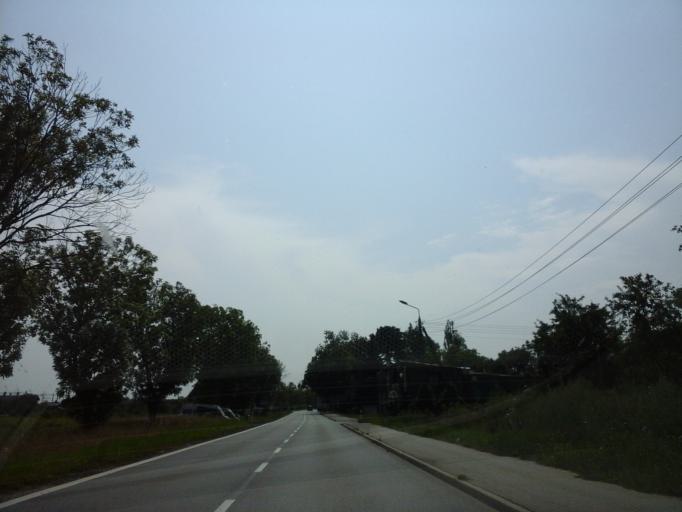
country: PL
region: Lower Silesian Voivodeship
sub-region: Powiat wroclawski
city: Zerniki Wroclawskie
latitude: 51.0323
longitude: 17.0652
